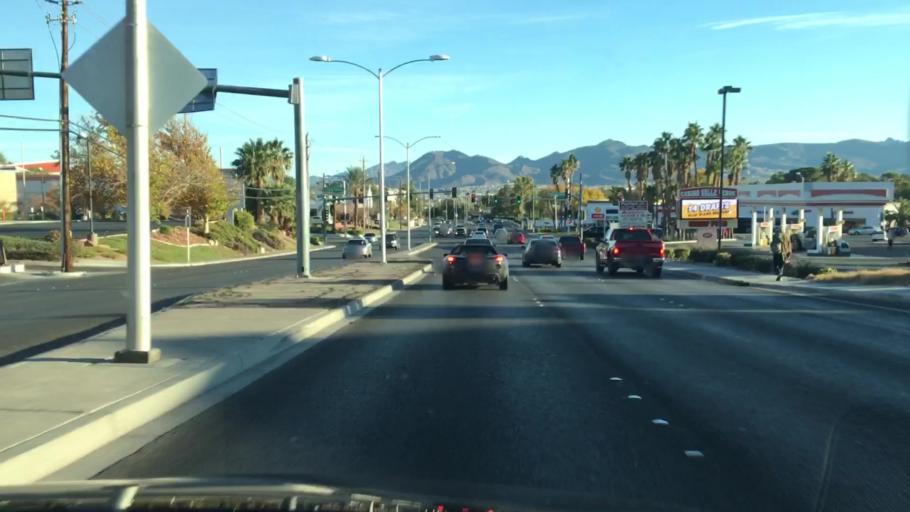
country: US
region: Nevada
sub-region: Clark County
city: Whitney
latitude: 36.0689
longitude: -115.0691
